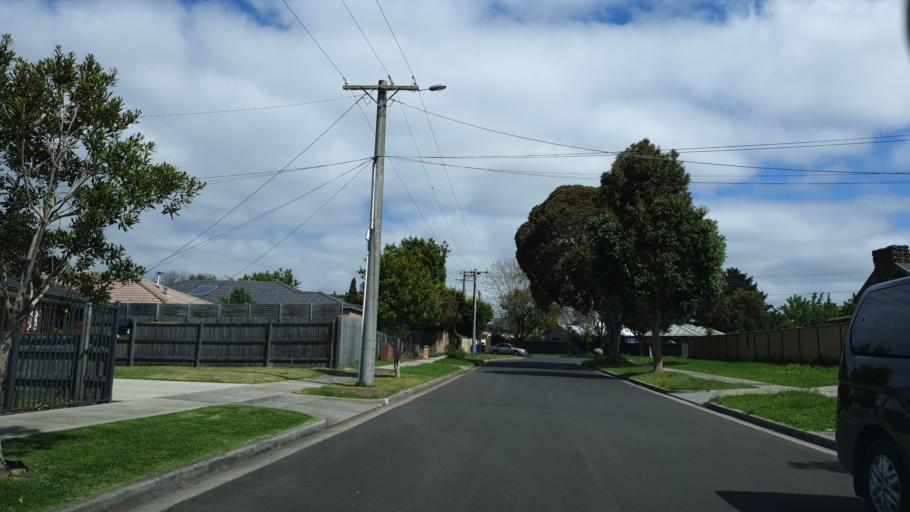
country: AU
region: Victoria
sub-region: Casey
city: Cranbourne
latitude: -38.1035
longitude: 145.2895
